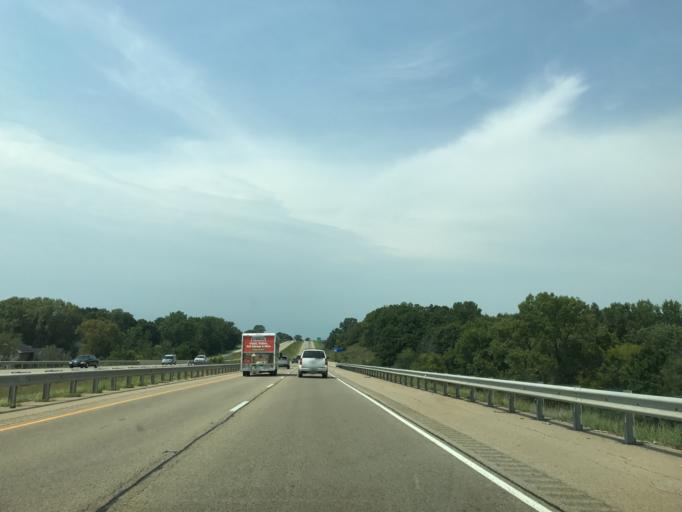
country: US
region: Illinois
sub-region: Bureau County
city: Ladd
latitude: 41.3645
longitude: -89.1849
